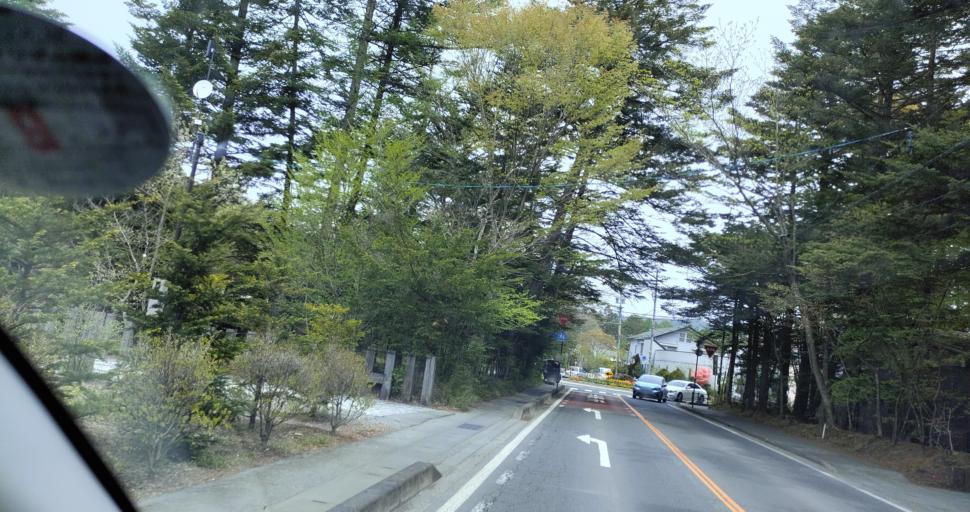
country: JP
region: Nagano
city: Saku
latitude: 36.3495
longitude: 138.6288
